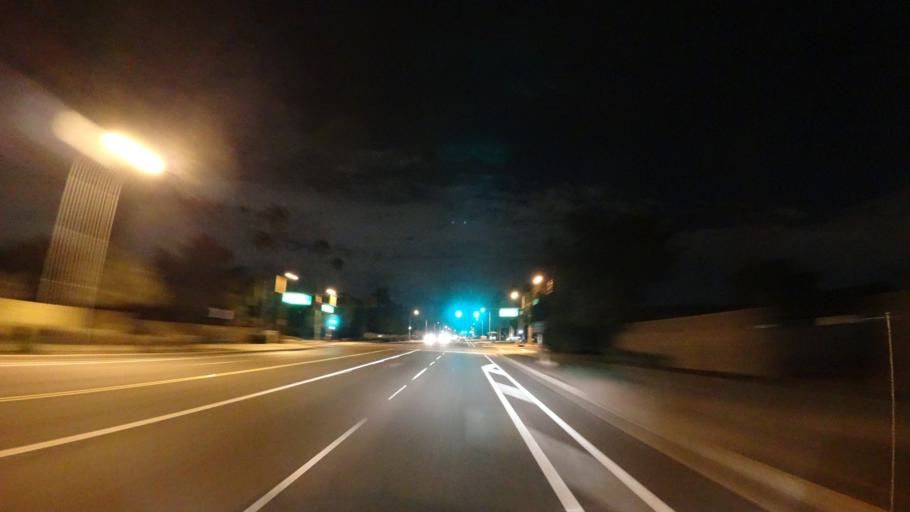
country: US
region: Arizona
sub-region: Maricopa County
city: Tempe
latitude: 33.3688
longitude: -111.9112
